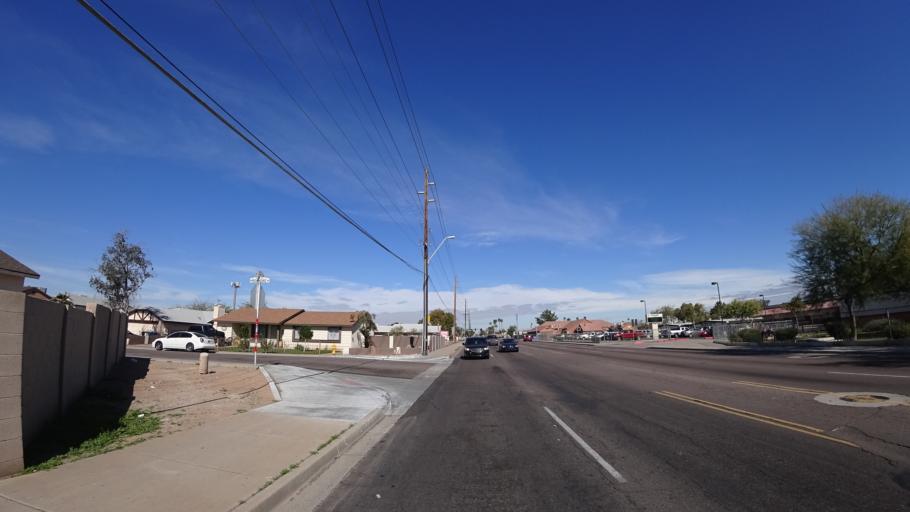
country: US
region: Arizona
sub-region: Maricopa County
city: Glendale
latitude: 33.4785
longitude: -112.1865
